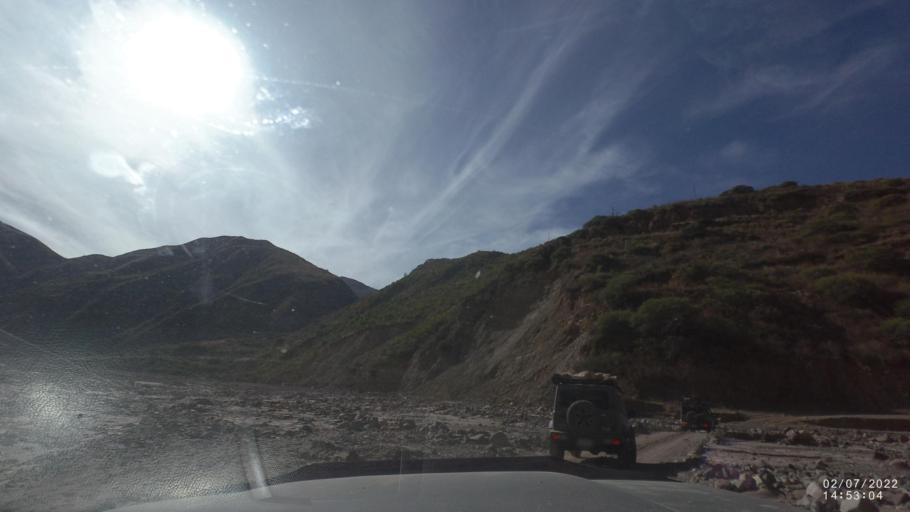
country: BO
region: Cochabamba
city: Irpa Irpa
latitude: -17.8531
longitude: -66.4341
